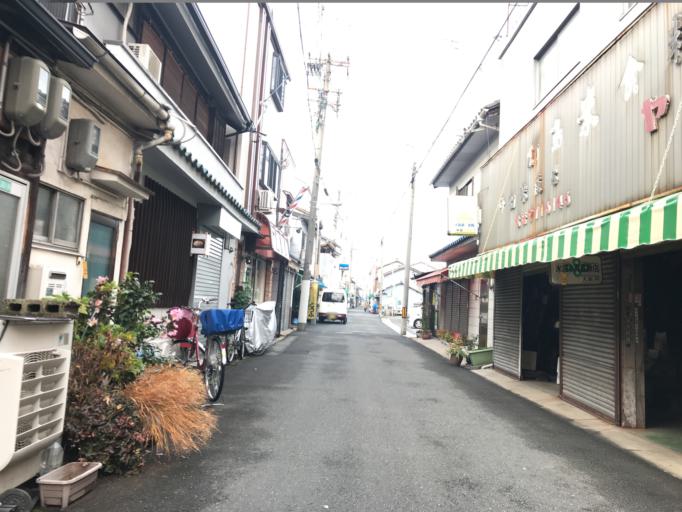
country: JP
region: Osaka
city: Osaka-shi
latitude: 34.6692
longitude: 135.5616
